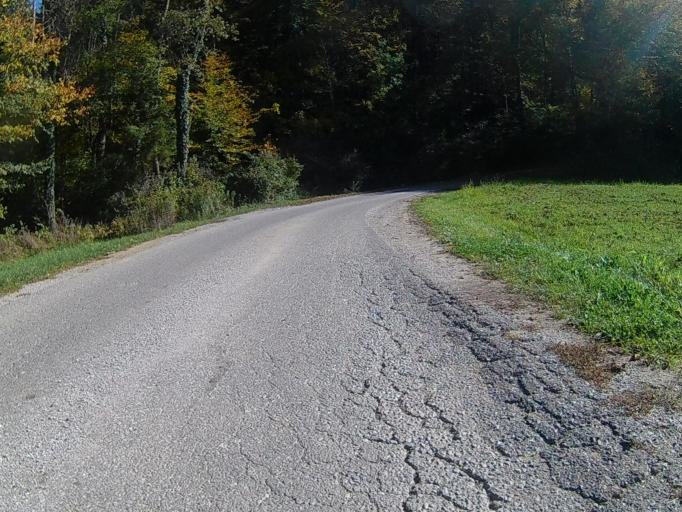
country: SI
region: Duplek
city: Spodnji Duplek
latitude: 46.5459
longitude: 15.7798
